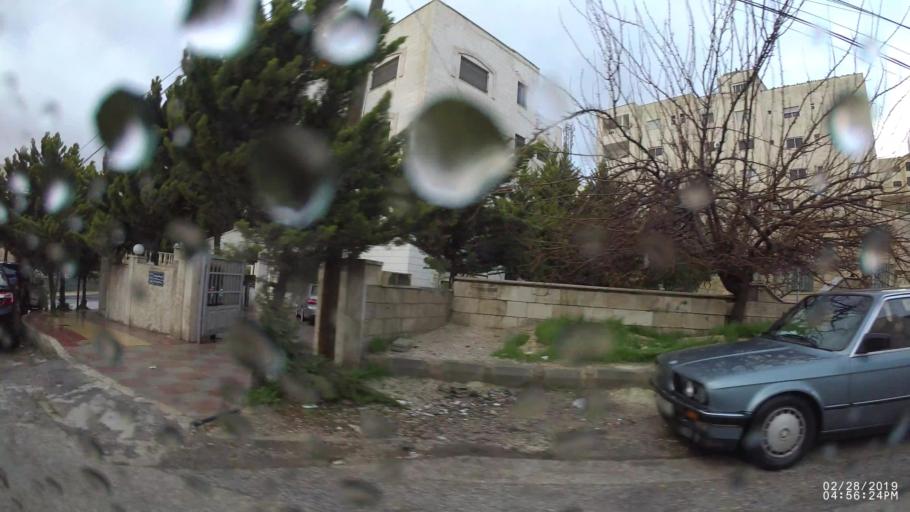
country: JO
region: Amman
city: Amman
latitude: 32.0020
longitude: 35.9300
